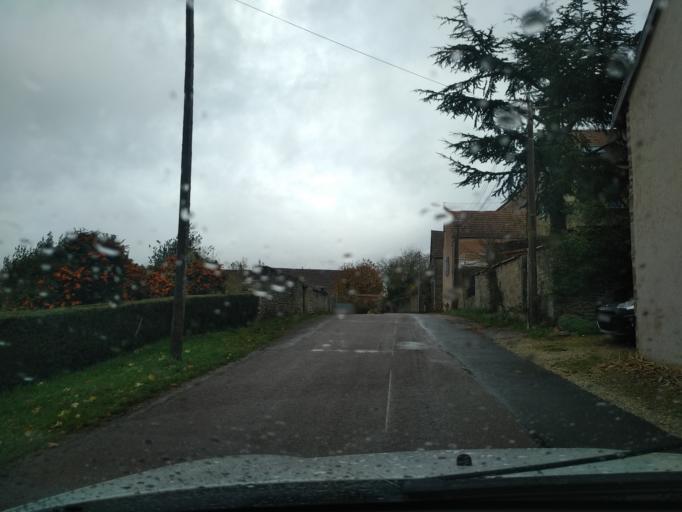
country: FR
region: Bourgogne
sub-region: Departement de Saone-et-Loire
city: Saint-Leger-sur-Dheune
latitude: 46.8474
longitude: 4.6851
